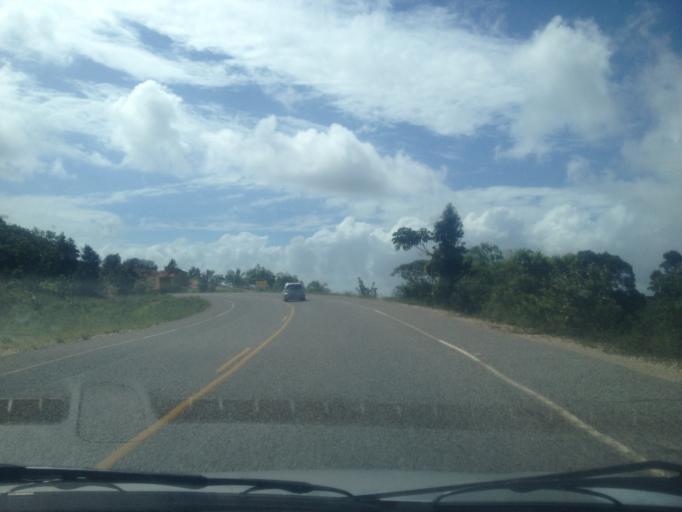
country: BR
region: Bahia
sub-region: Conde
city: Conde
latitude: -11.7178
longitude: -37.5727
